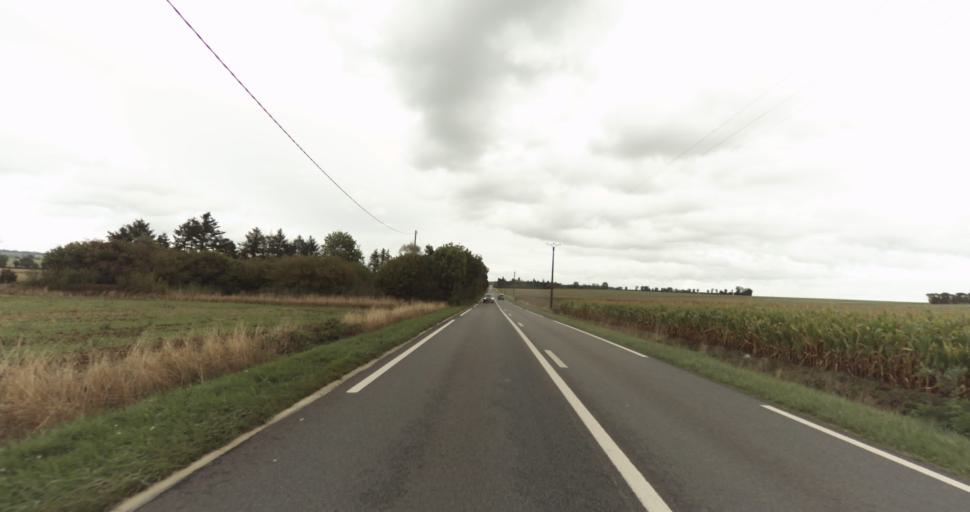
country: FR
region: Lower Normandy
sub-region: Departement de l'Orne
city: Gace
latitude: 48.7017
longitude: 0.2577
